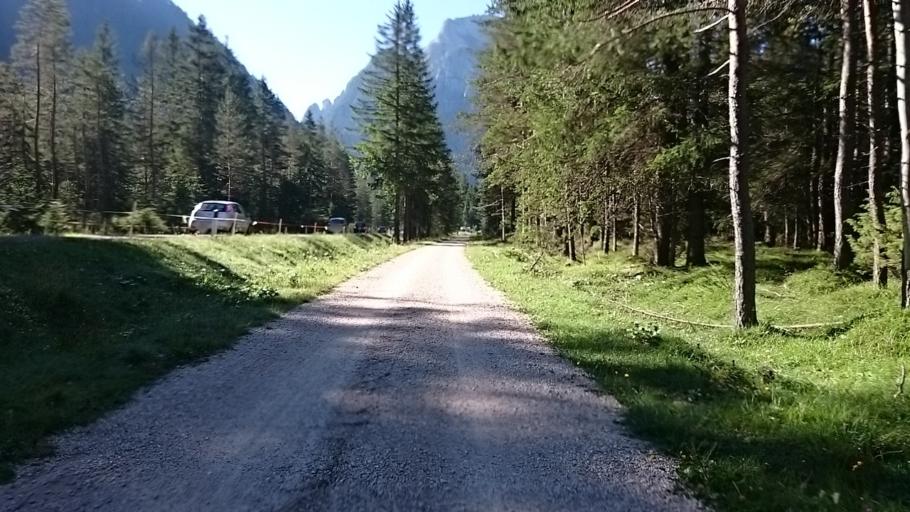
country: IT
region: Trentino-Alto Adige
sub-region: Bolzano
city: Dobbiaco
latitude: 46.6476
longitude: 12.2311
